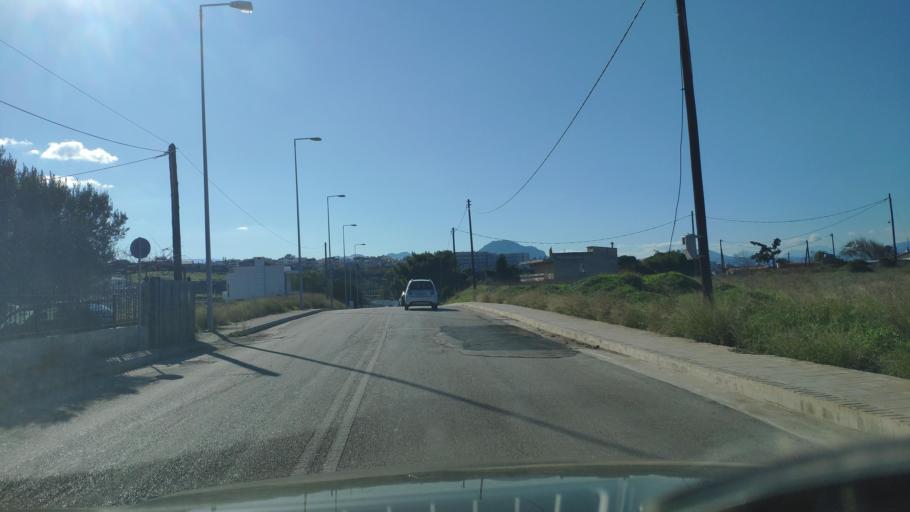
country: GR
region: Peloponnese
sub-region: Nomos Korinthias
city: Korinthos
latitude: 37.9449
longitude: 22.9553
